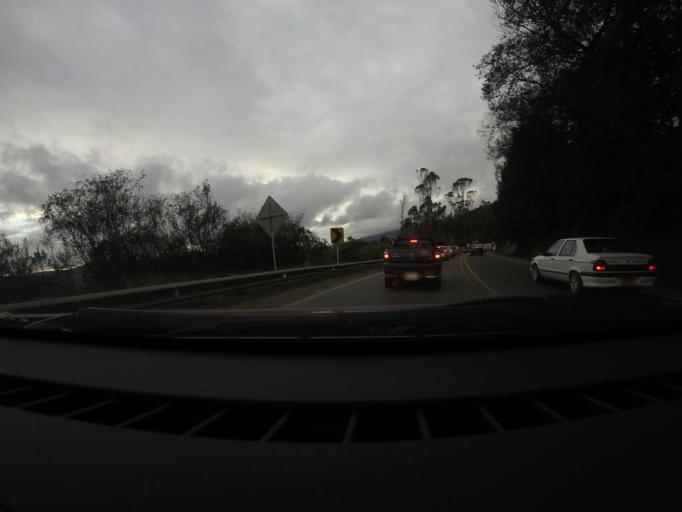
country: CO
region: Boyaca
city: Samaca
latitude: 5.4598
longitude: -73.4172
